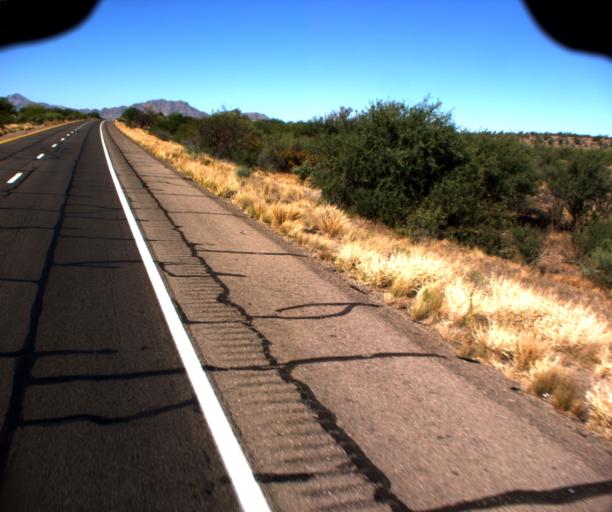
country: US
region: Arizona
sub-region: Pima County
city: Arivaca Junction
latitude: 31.7423
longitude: -111.0485
